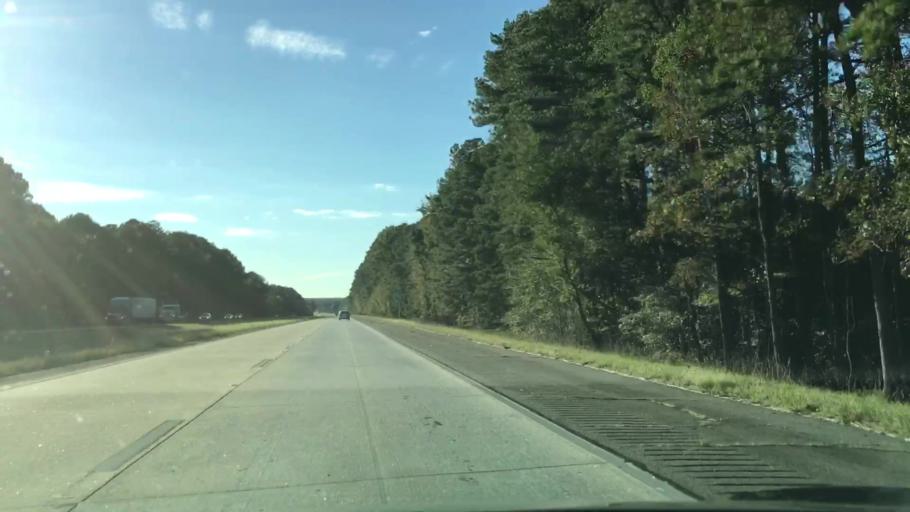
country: US
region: Georgia
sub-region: Greene County
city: Greensboro
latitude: 33.5478
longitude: -83.1150
